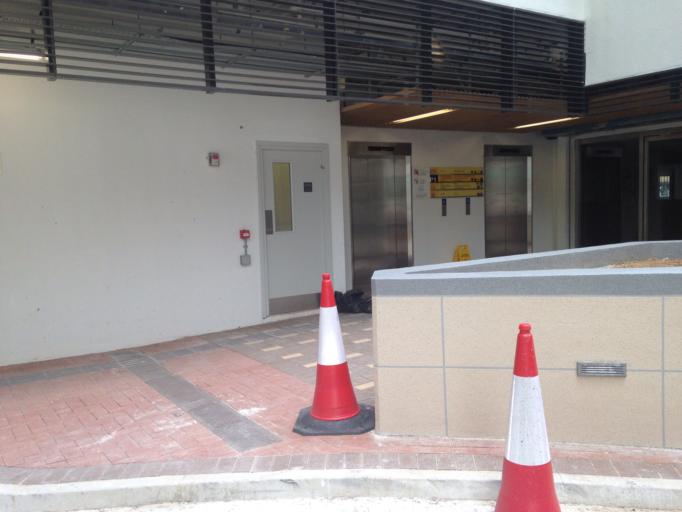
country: HK
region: Tai Po
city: Tai Po
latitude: 22.4469
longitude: 114.1657
